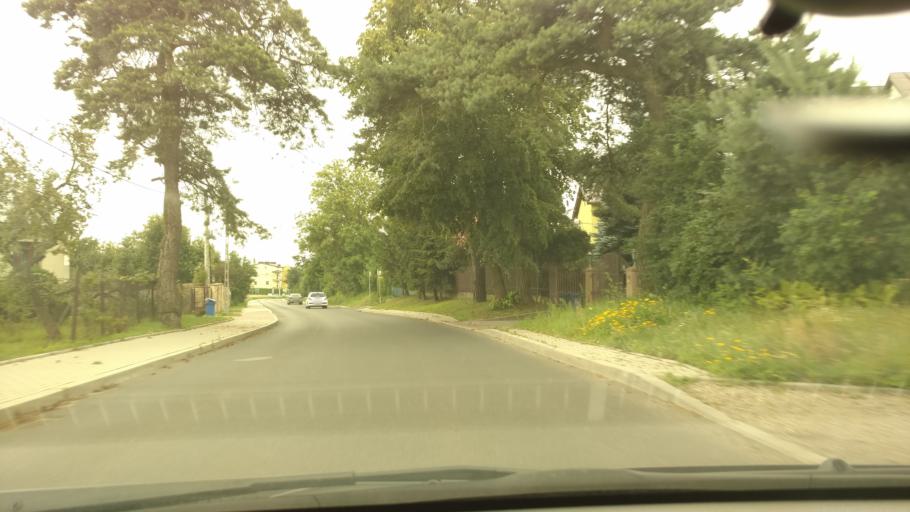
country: PL
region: Lesser Poland Voivodeship
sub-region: Powiat krakowski
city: Zielonki
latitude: 50.1212
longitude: 19.9401
